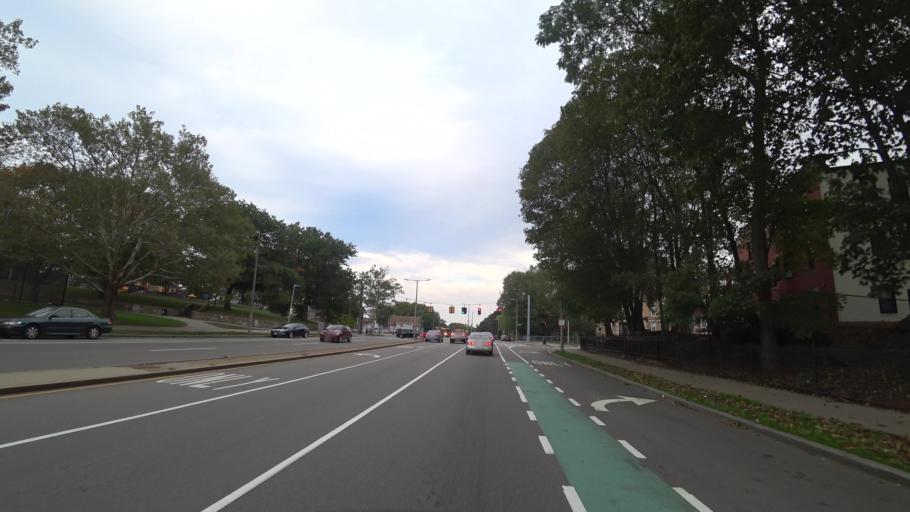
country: US
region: Massachusetts
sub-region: Suffolk County
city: Jamaica Plain
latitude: 42.3203
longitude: -71.0894
